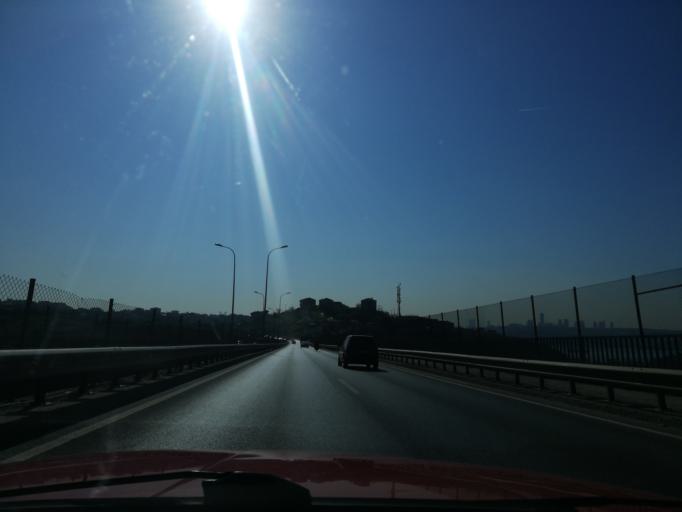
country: TR
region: Istanbul
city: Umraniye
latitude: 41.1055
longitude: 29.1030
